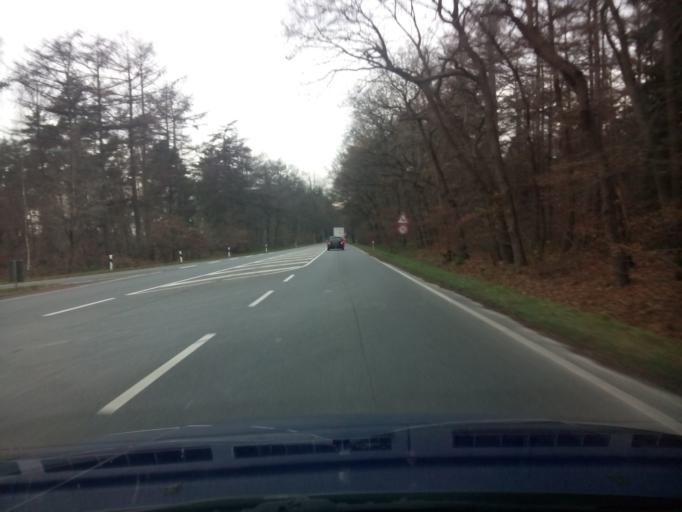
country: DE
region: Lower Saxony
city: Elmlohe
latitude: 53.6186
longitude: 8.7013
